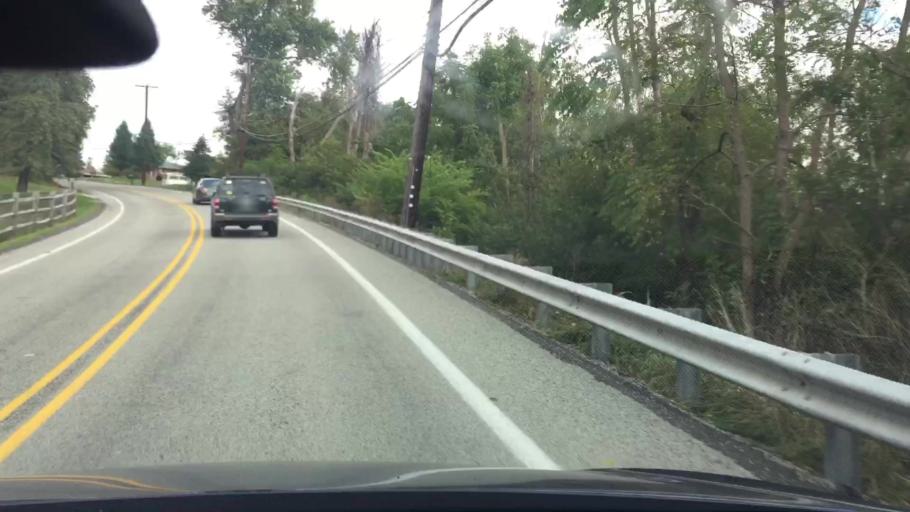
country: US
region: Pennsylvania
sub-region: Allegheny County
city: Penn Hills
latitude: 40.4974
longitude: -79.7985
